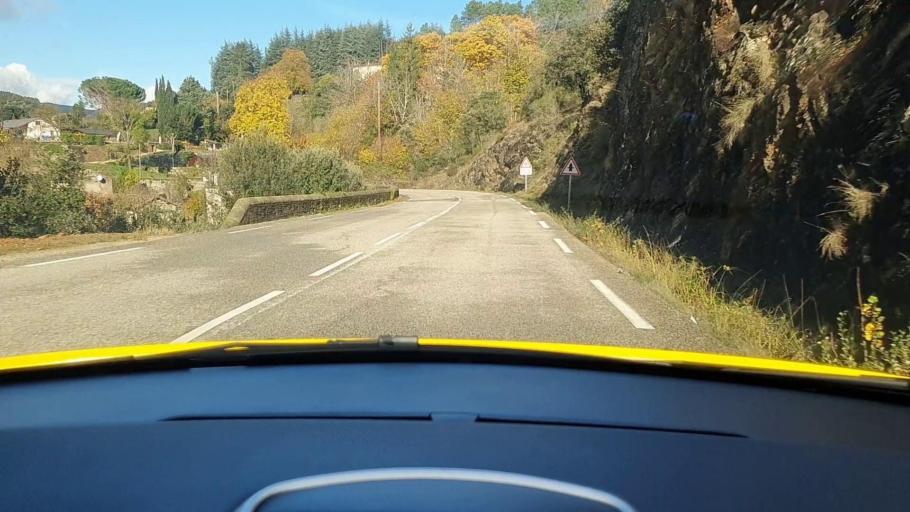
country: FR
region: Languedoc-Roussillon
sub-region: Departement du Gard
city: Valleraugue
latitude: 44.1413
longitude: 3.7030
